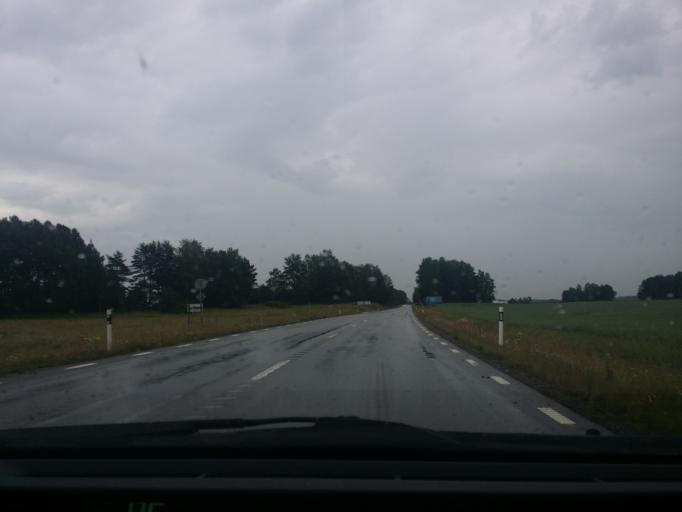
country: SE
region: OErebro
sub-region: Lindesbergs Kommun
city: Fellingsbro
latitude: 59.4693
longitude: 15.5424
